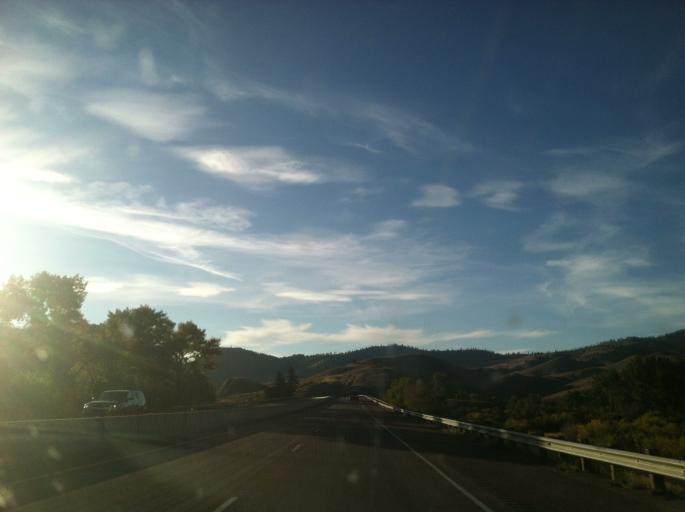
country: US
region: Montana
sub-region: Granite County
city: Philipsburg
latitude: 46.7111
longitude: -113.2652
